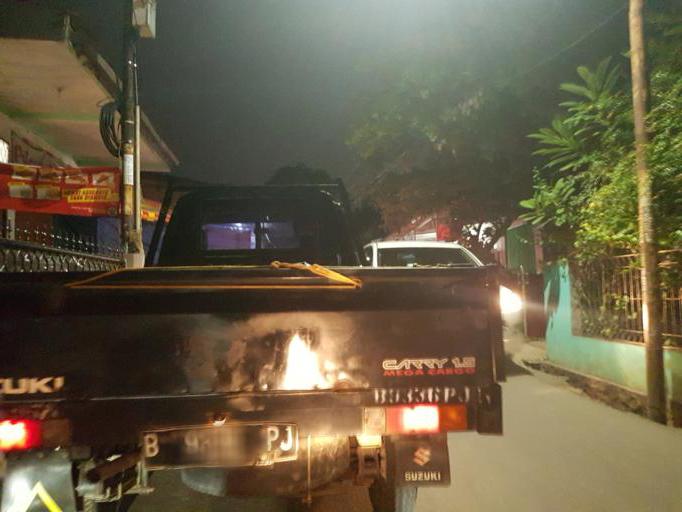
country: ID
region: West Java
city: Cileungsir
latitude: -6.3172
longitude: 106.9179
